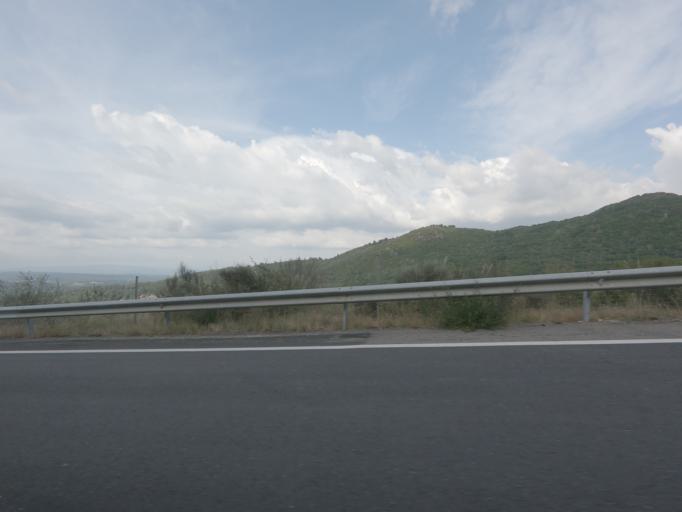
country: ES
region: Galicia
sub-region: Provincia de Ourense
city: Ambia
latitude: 42.1831
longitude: -7.7650
